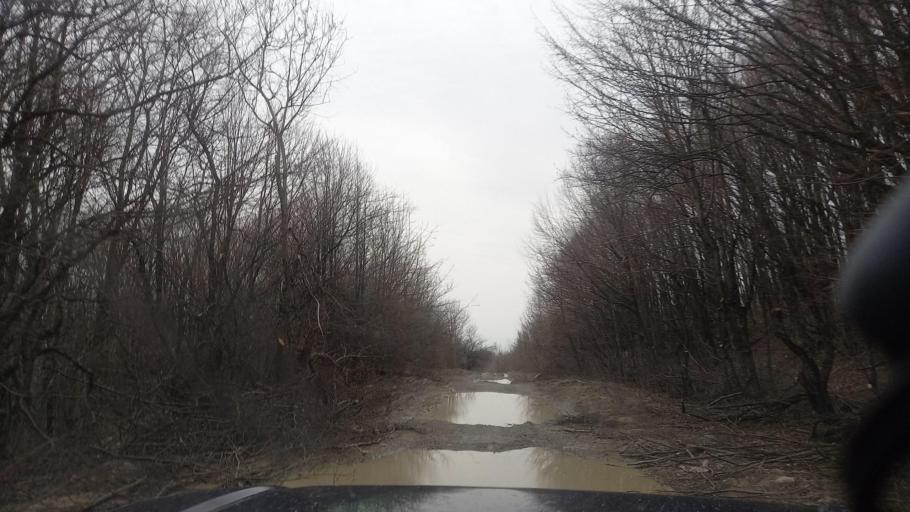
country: RU
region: Krasnodarskiy
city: Pshada
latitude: 44.5964
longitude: 38.2908
